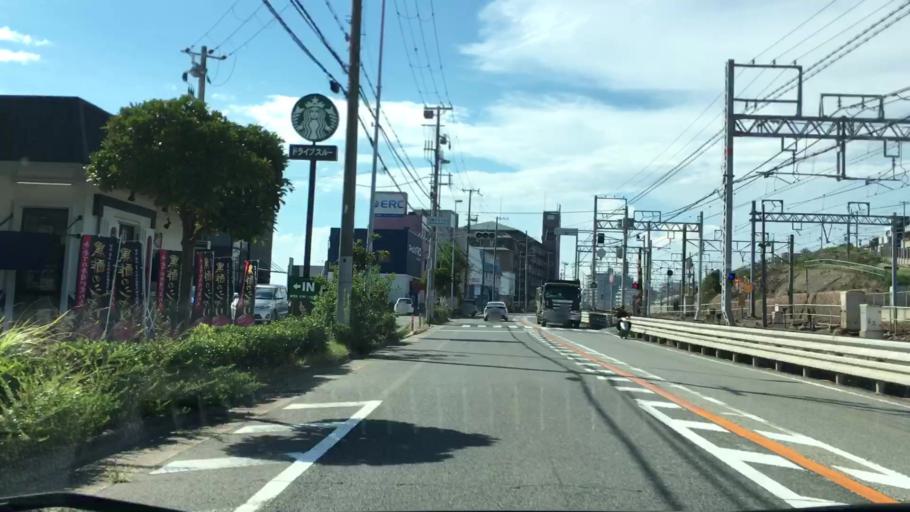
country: JP
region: Hyogo
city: Akashi
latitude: 34.6398
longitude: 135.0256
